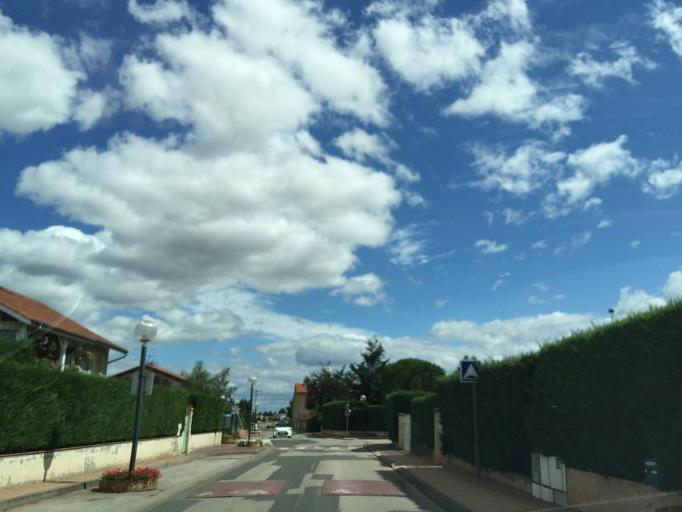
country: FR
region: Rhone-Alpes
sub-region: Departement de la Loire
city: Savigneux
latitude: 45.6109
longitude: 4.0850
